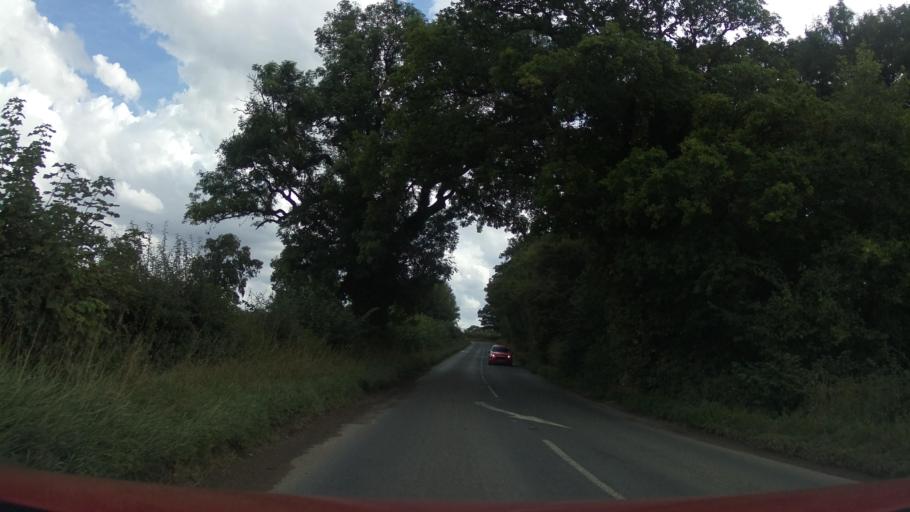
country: GB
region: England
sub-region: North Yorkshire
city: Bedale
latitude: 54.2243
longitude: -1.6395
